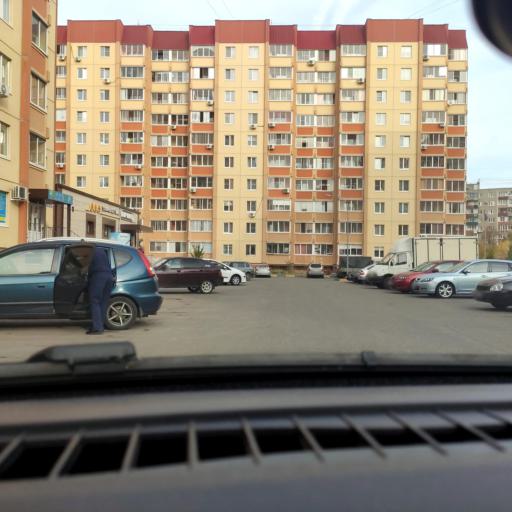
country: RU
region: Voronezj
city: Voronezh
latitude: 51.7175
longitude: 39.2649
